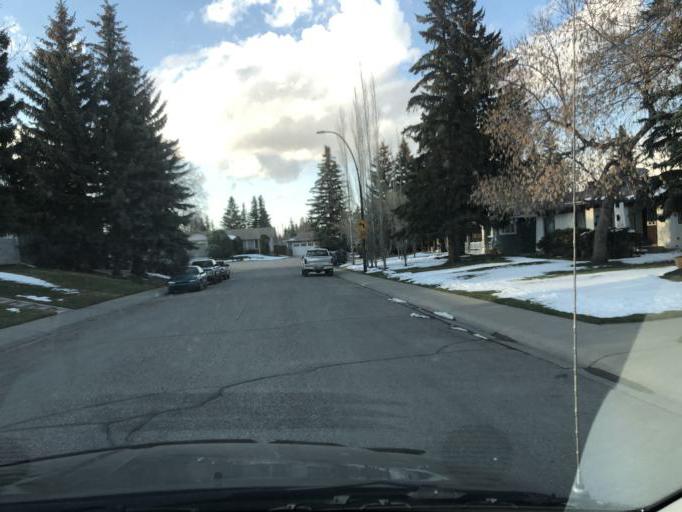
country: CA
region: Alberta
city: Calgary
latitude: 50.9411
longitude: -114.0362
